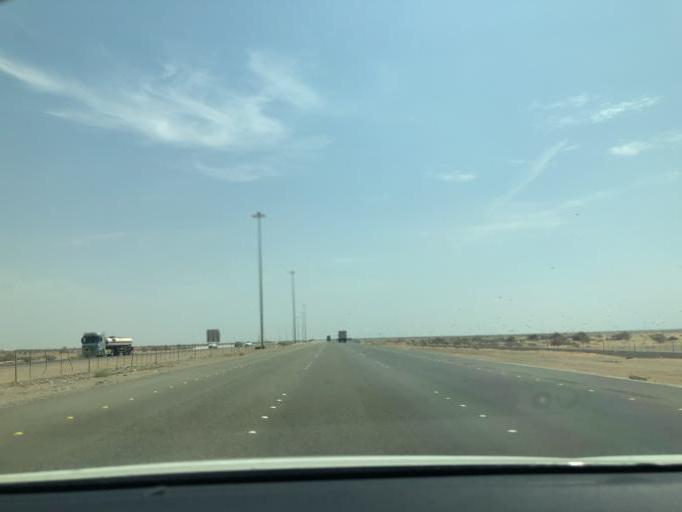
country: SA
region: Makkah
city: Rabigh
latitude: 22.2549
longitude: 39.1172
